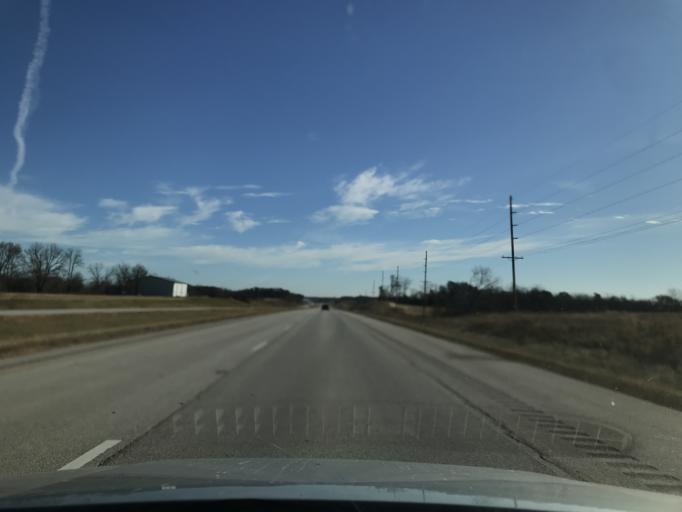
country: US
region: Illinois
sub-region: Hancock County
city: Carthage
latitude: 40.4146
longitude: -91.0404
